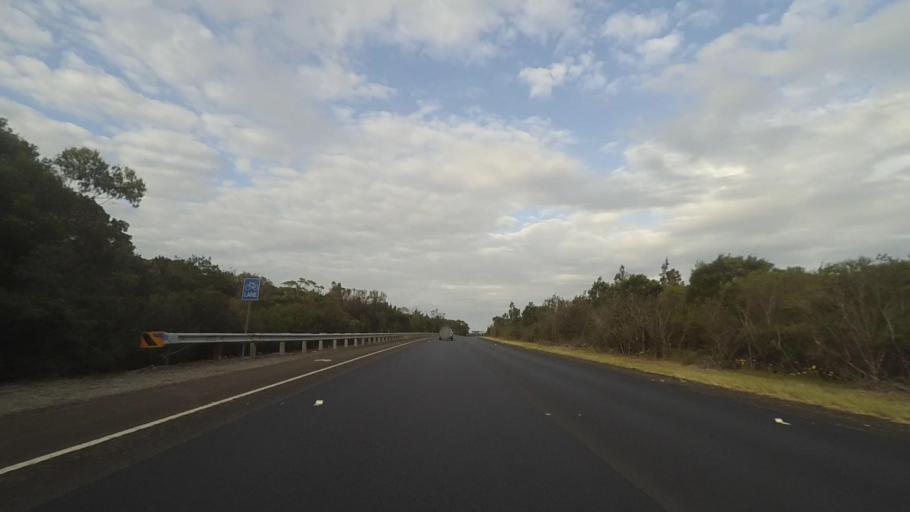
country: AU
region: New South Wales
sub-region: Wollongong
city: Helensburgh
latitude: -34.2464
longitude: 150.9382
